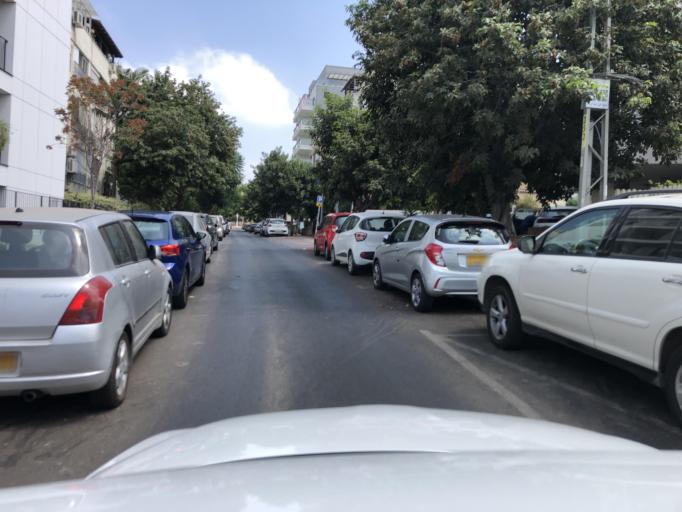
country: IL
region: Tel Aviv
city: Giv`atayim
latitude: 32.0766
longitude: 34.8121
